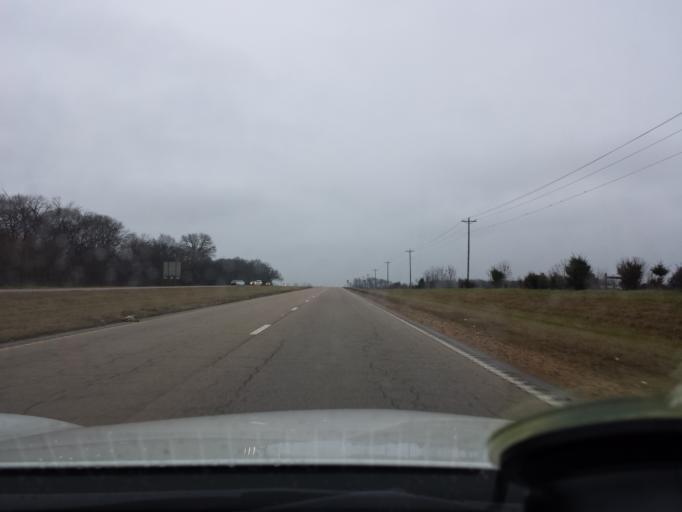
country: US
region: Mississippi
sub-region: Chickasaw County
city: Okolona
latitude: 34.0191
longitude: -88.7016
